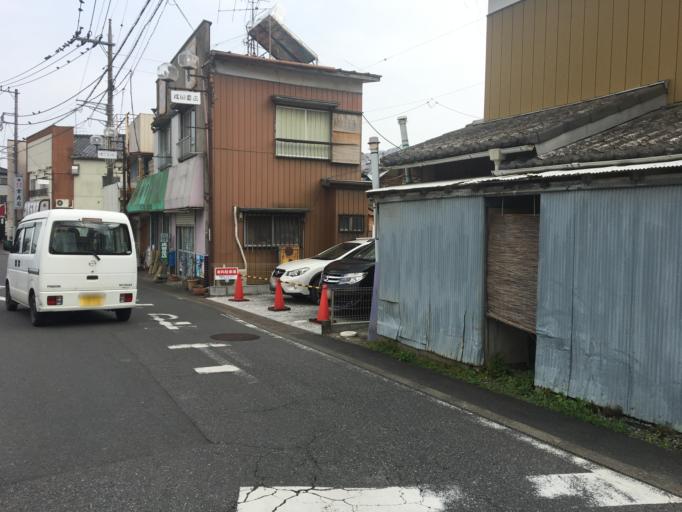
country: JP
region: Saitama
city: Sugito
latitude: 36.0261
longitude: 139.7272
